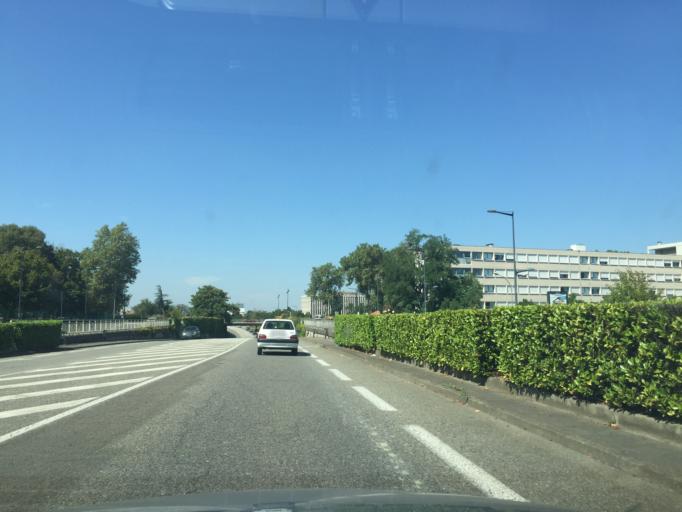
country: FR
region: Midi-Pyrenees
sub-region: Departement de la Haute-Garonne
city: Ramonville-Saint-Agne
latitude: 43.5618
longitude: 1.4623
